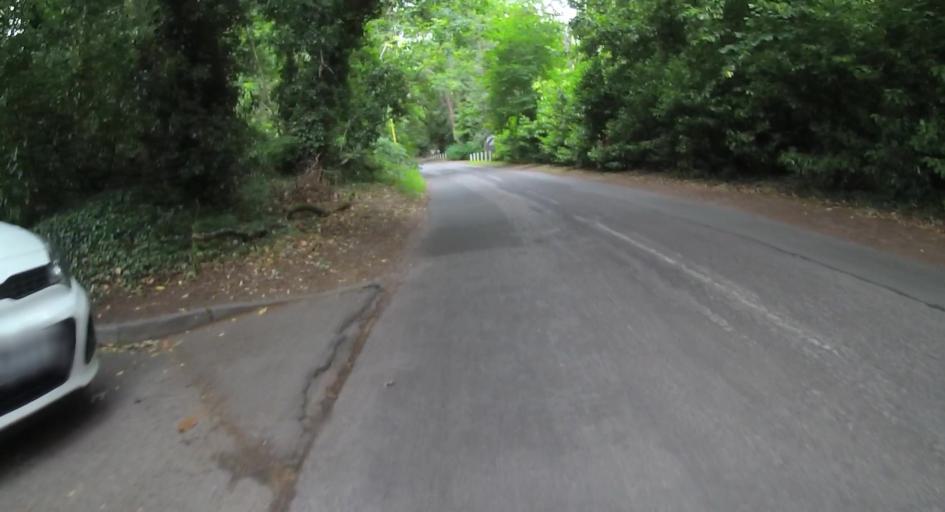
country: GB
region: England
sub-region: Surrey
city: Seale
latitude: 51.2093
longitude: -0.7375
